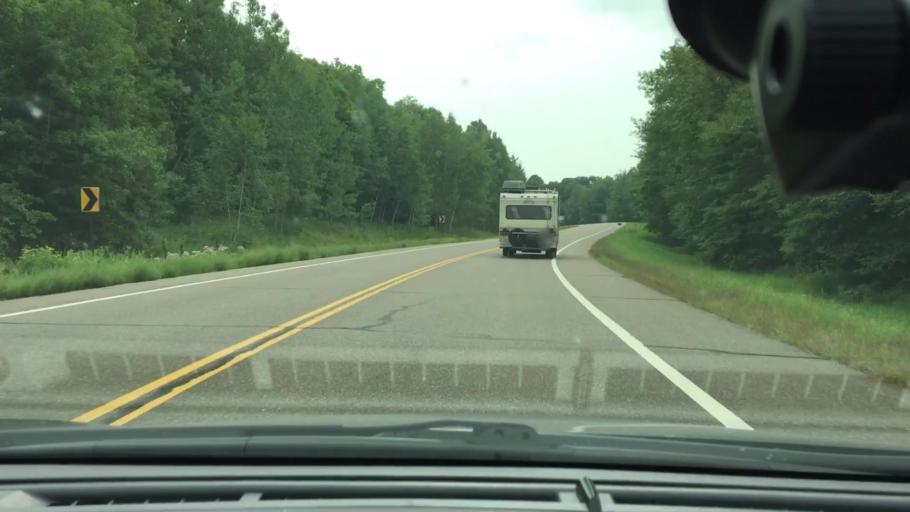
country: US
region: Minnesota
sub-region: Crow Wing County
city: Crosby
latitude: 46.4105
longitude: -93.8246
